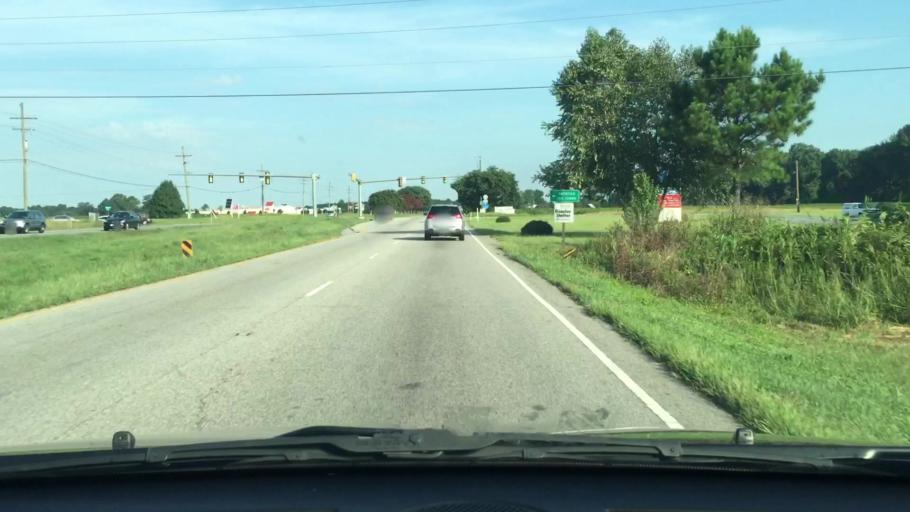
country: US
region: Virginia
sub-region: Isle of Wight County
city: Carrollton
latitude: 36.9487
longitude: -76.5956
